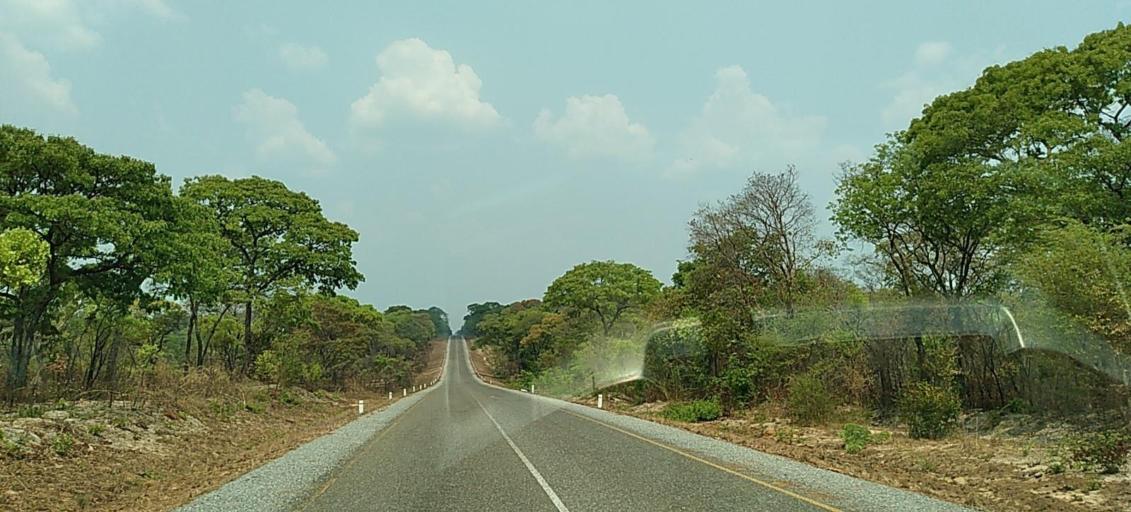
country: ZM
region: North-Western
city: Zambezi
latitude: -13.5668
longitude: 23.2235
